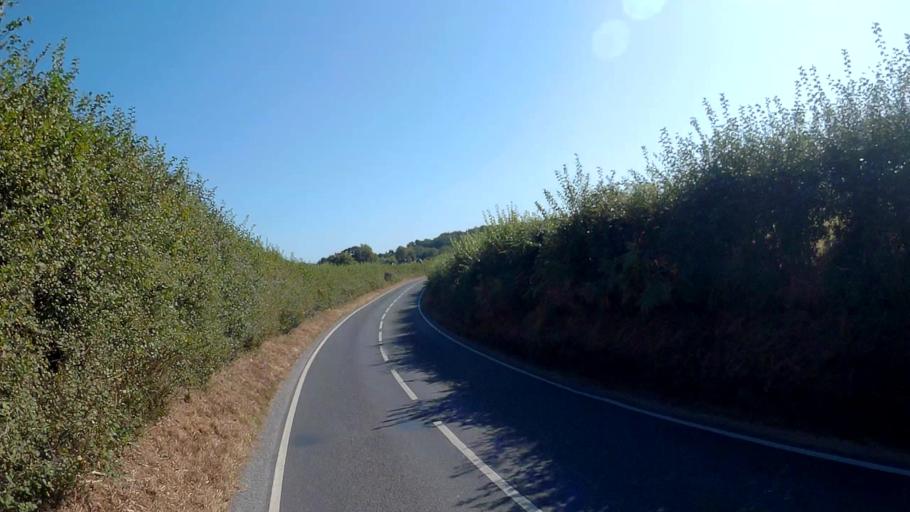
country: GB
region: England
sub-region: Surrey
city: Farnham
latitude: 51.1877
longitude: -0.7590
